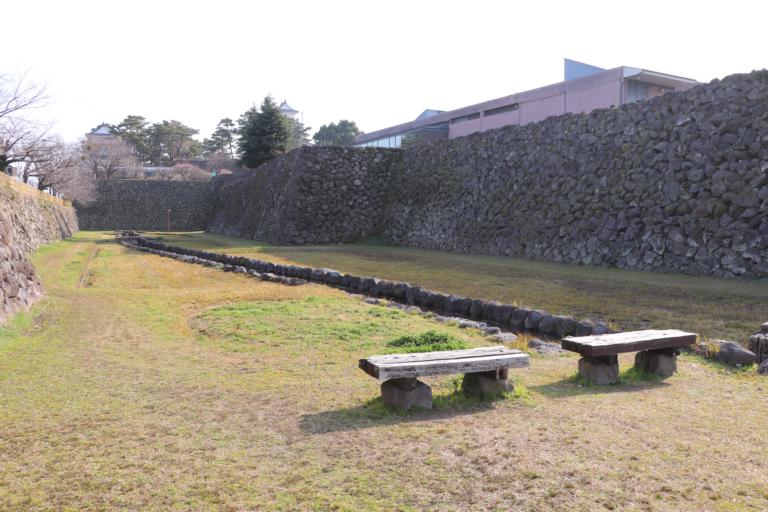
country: JP
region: Nagasaki
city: Shimabara
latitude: 32.7917
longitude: 130.3670
